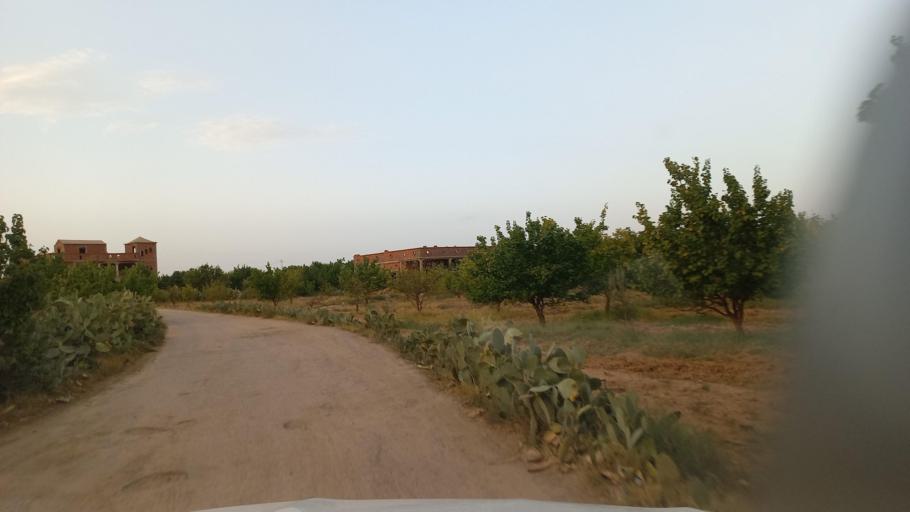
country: TN
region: Al Qasrayn
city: Kasserine
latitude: 35.2738
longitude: 9.0536
